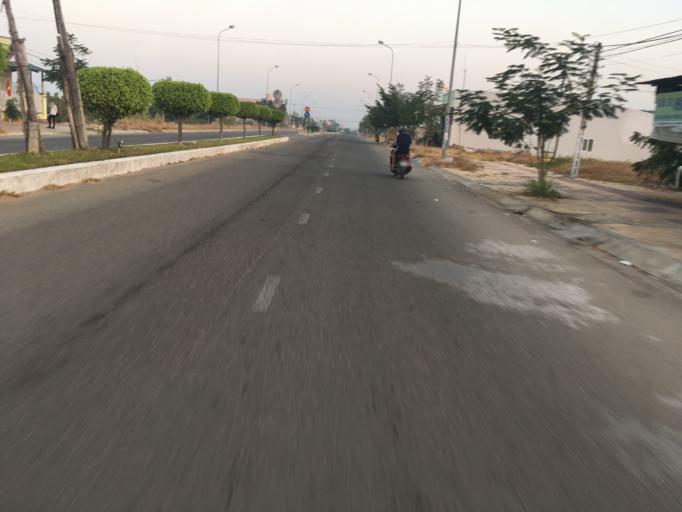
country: VN
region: Ninh Thuan
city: Phan Rang-Thap Cham
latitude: 11.5558
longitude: 109.0231
